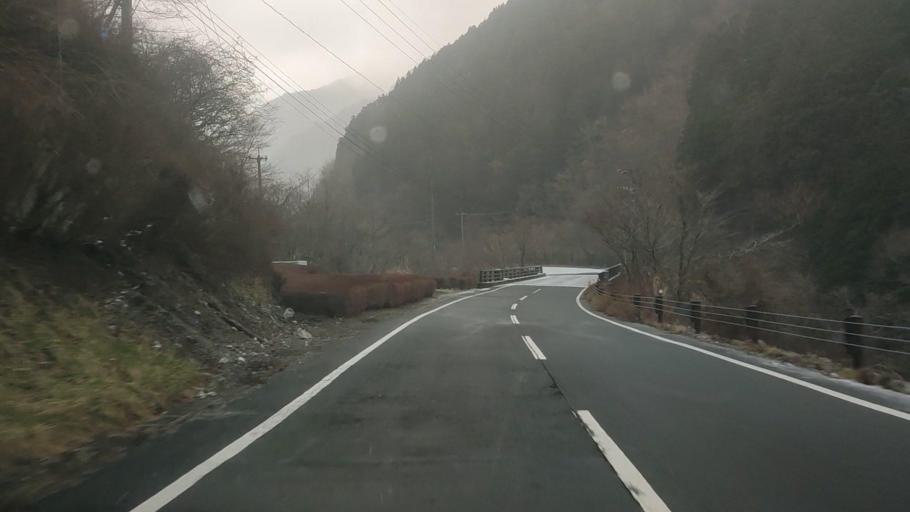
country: JP
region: Kumamoto
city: Matsubase
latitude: 32.5605
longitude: 130.9169
